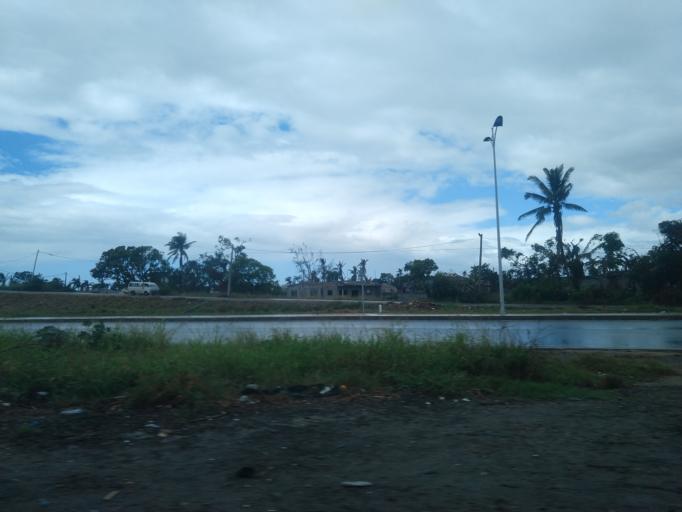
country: MZ
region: Sofala
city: Beira
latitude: -19.7836
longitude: 34.8773
